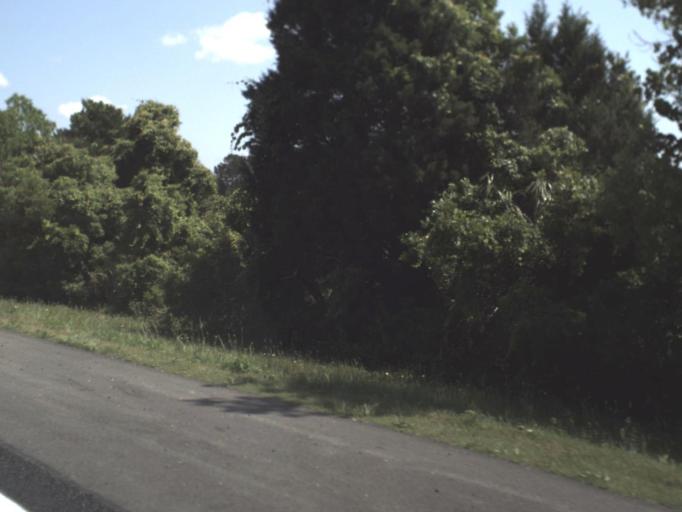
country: US
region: Florida
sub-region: Nassau County
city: Yulee
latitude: 30.5780
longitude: -81.6463
